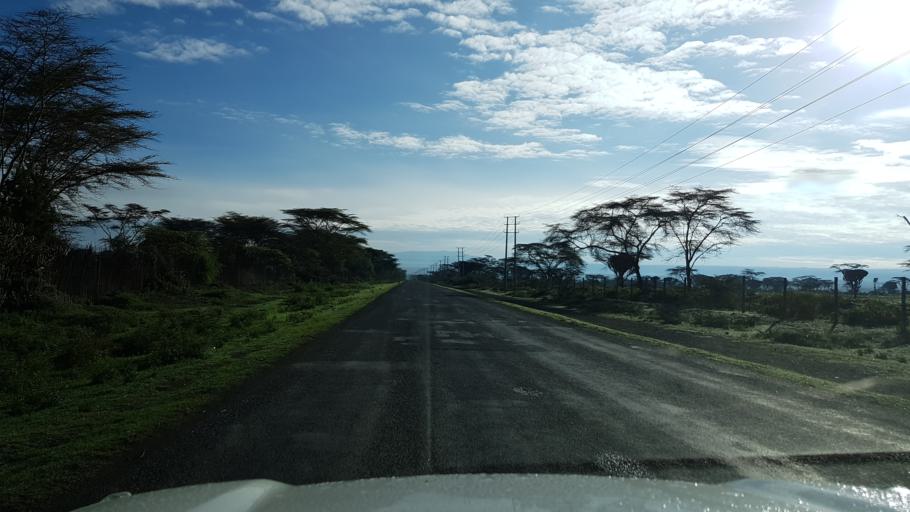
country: KE
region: Nakuru
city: Naivasha
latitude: -0.8128
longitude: 36.4001
